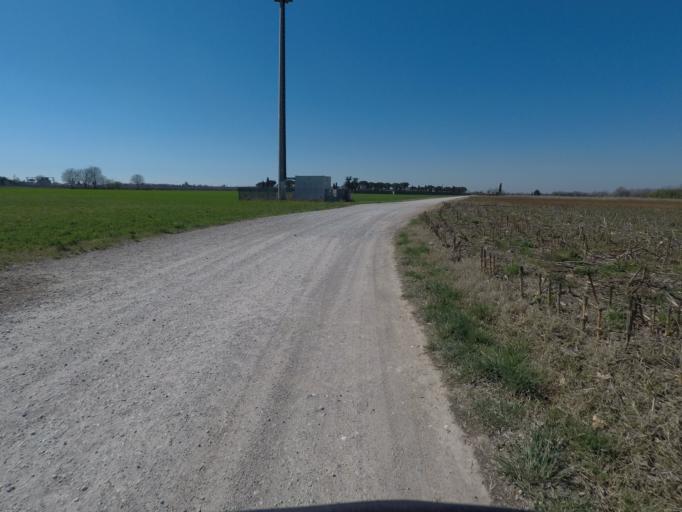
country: IT
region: Friuli Venezia Giulia
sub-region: Provincia di Gorizia
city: Gradisca d'Isonzo
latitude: 45.9025
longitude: 13.4898
